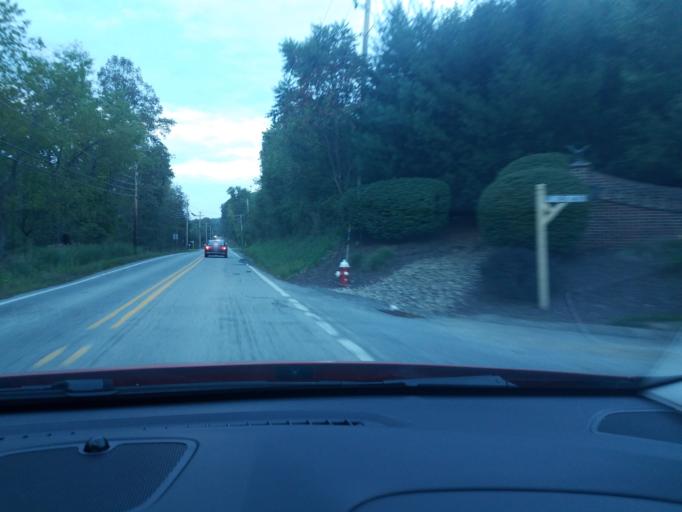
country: US
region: Pennsylvania
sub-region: Allegheny County
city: Bradford Woods
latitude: 40.6218
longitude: -80.0781
